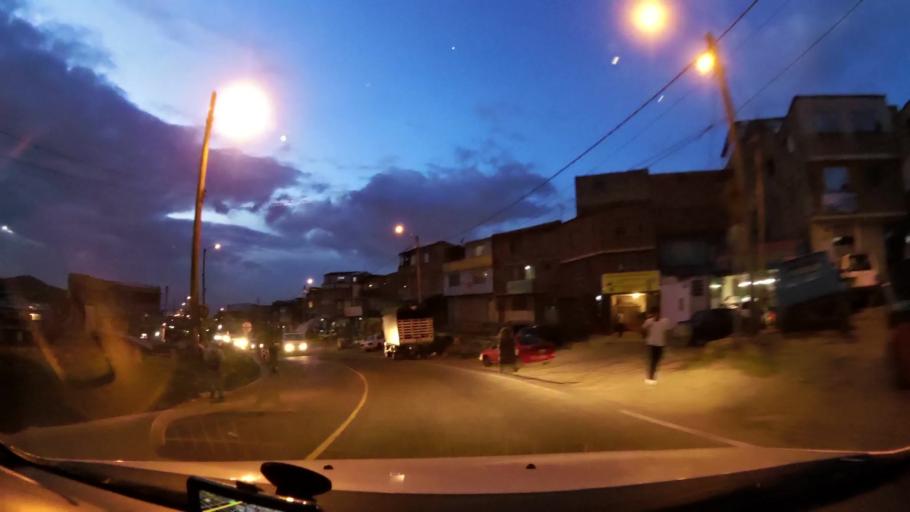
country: CO
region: Bogota D.C.
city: Bogota
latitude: 4.5531
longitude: -74.0905
